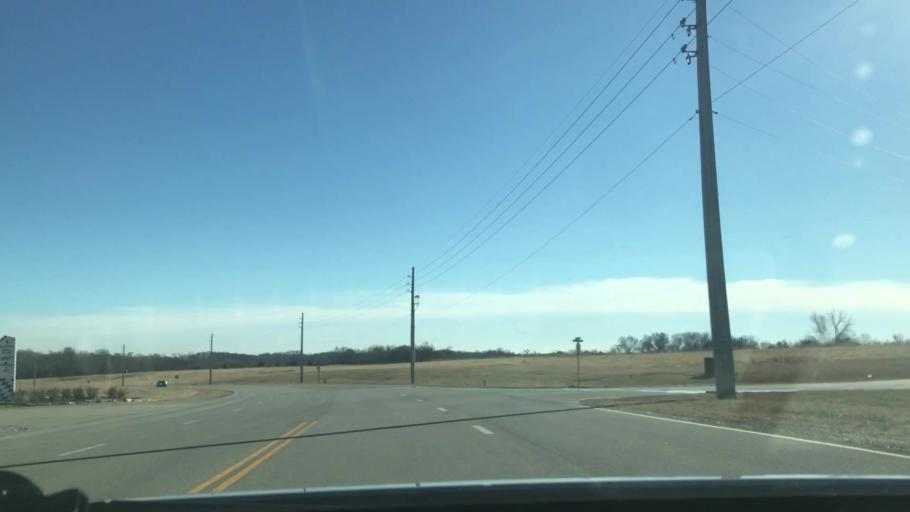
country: US
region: Kansas
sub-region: Wyandotte County
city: Edwardsville
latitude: 39.1106
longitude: -94.8527
